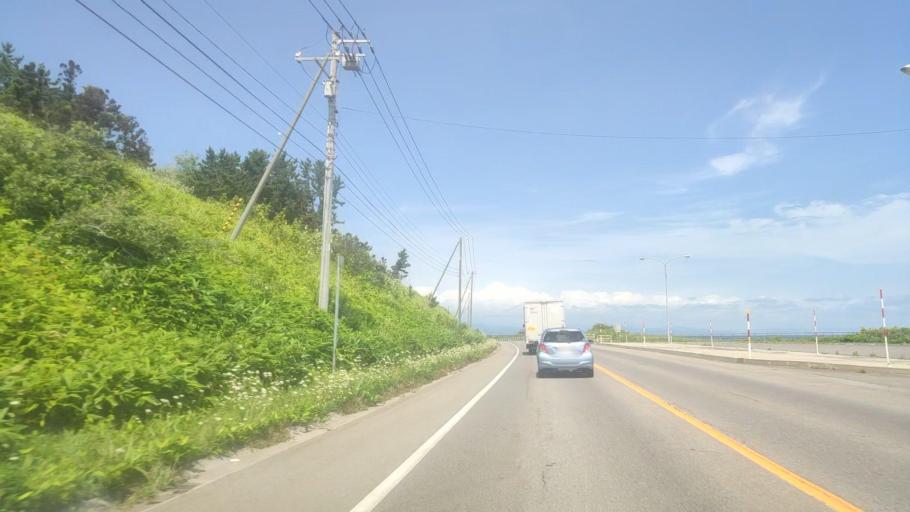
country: JP
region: Hokkaido
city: Nanae
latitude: 42.2041
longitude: 140.4063
